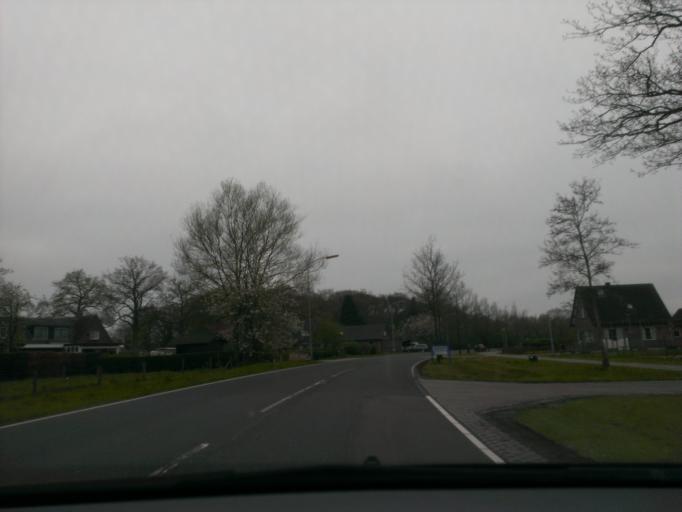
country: NL
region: Gelderland
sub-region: Gemeente Epe
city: Vaassen
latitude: 52.2932
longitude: 5.9876
